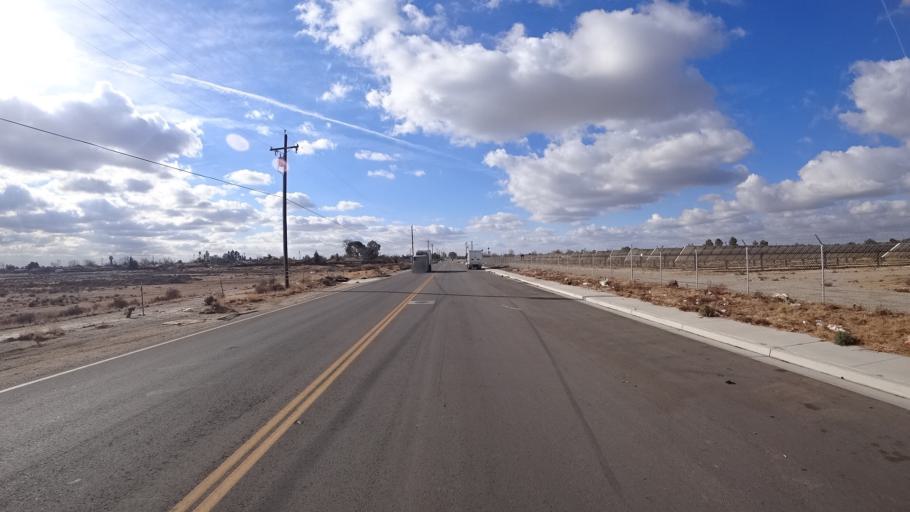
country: US
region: California
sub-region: Kern County
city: Greenfield
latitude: 35.3250
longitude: -118.9786
